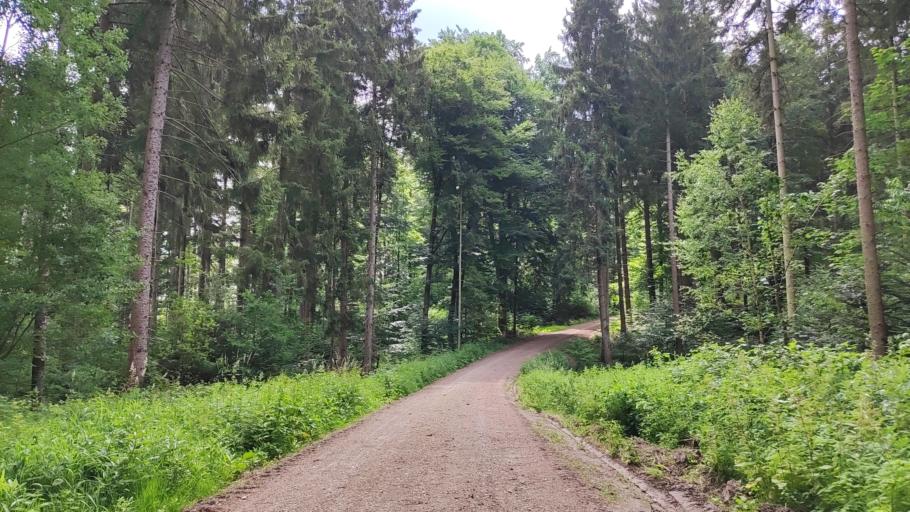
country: DE
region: Bavaria
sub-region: Swabia
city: Adelsried
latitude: 48.4146
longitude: 10.7075
